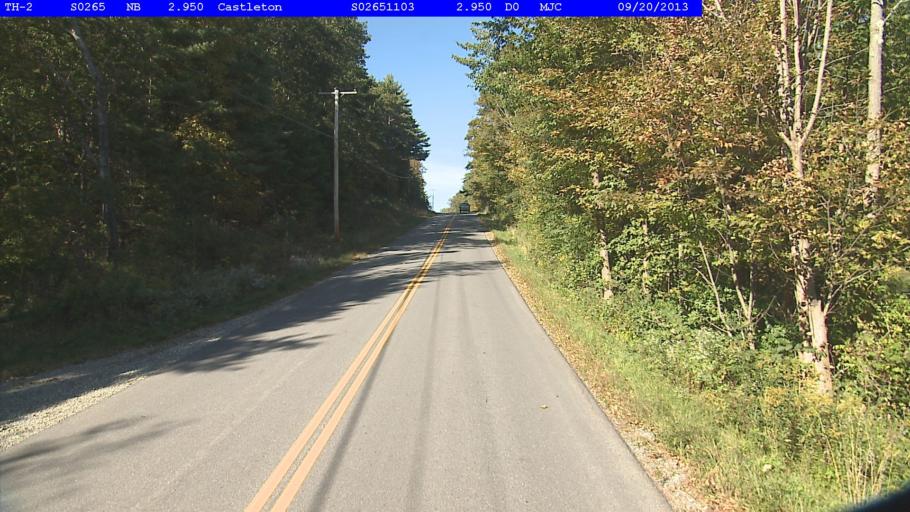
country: US
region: Vermont
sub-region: Rutland County
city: Fair Haven
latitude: 43.6432
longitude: -73.2335
